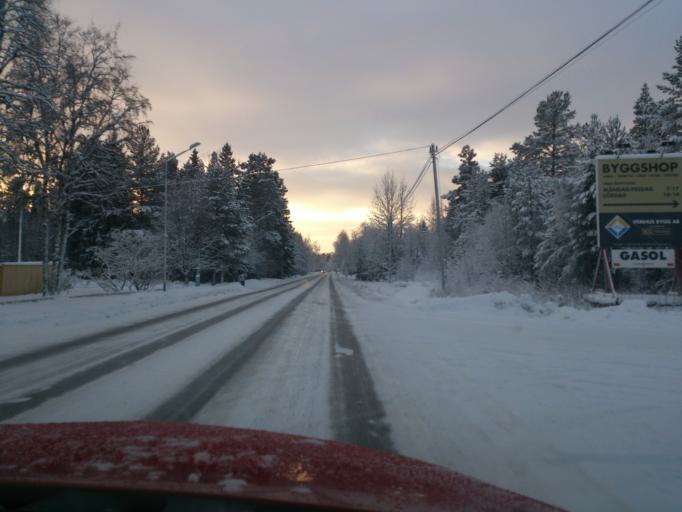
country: SE
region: Jaemtland
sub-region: Harjedalens Kommun
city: Sveg
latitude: 62.4636
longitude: 13.8682
